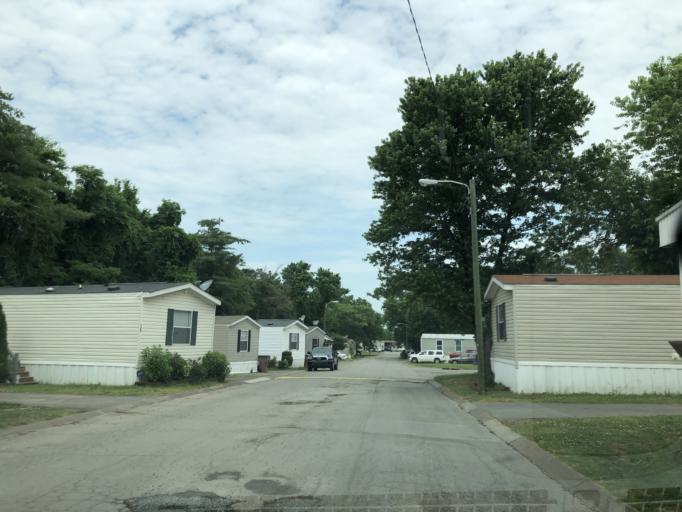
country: US
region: Tennessee
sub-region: Davidson County
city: Oak Hill
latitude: 36.0715
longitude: -86.6778
